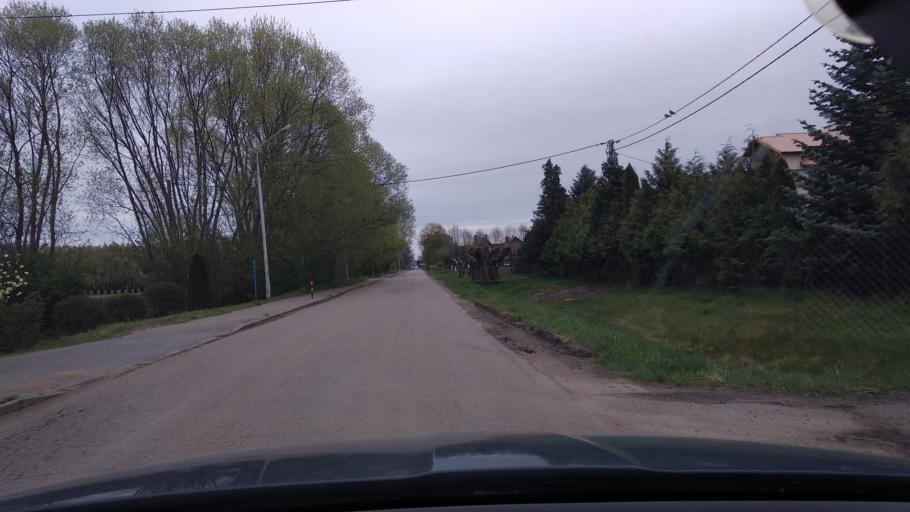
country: PL
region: Pomeranian Voivodeship
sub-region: Powiat gdanski
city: Pruszcz Gdanski
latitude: 54.2760
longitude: 18.6738
